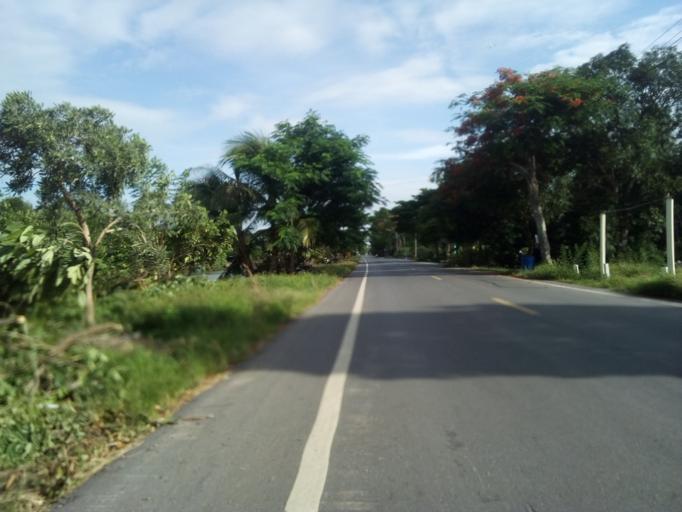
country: TH
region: Pathum Thani
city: Nong Suea
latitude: 14.0950
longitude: 100.8461
